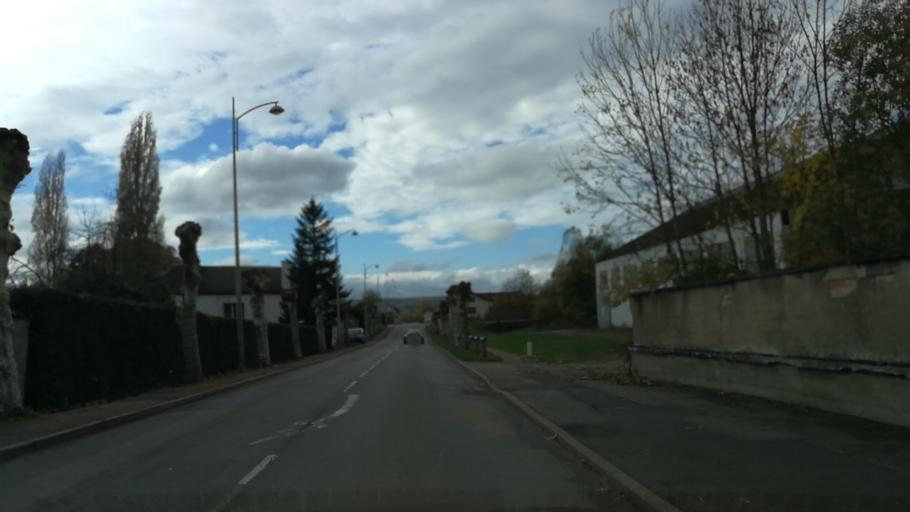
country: FR
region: Bourgogne
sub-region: Departement de la Cote-d'Or
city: Pouilly-en-Auxois
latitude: 47.2689
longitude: 4.5459
